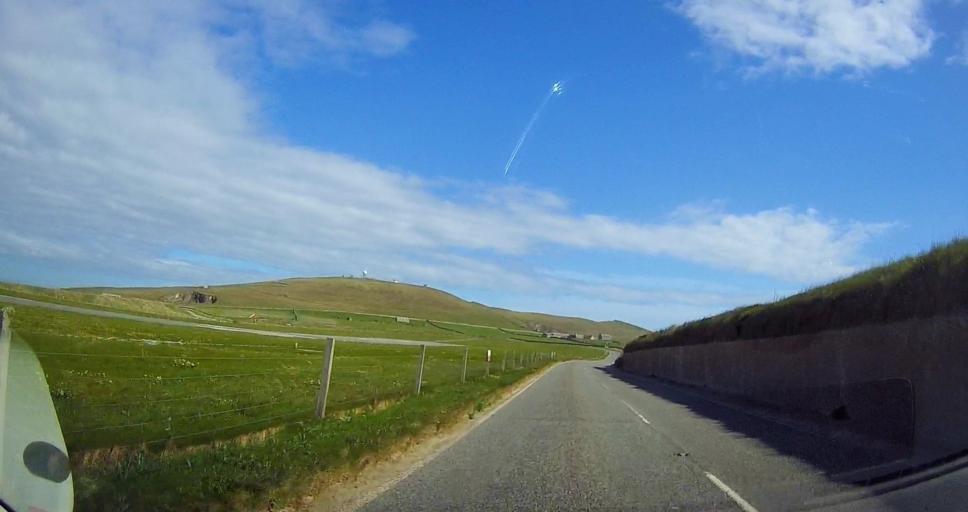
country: GB
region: Scotland
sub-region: Shetland Islands
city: Sandwick
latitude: 59.8738
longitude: -1.2900
